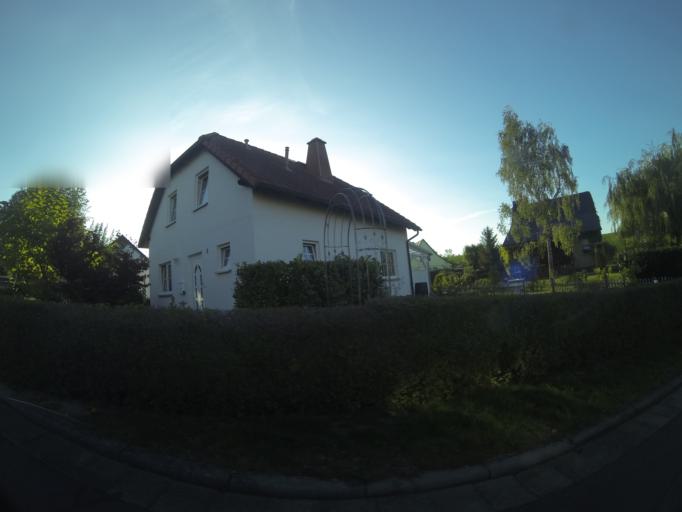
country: DE
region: Thuringia
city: Schmolln
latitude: 50.8915
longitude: 12.3715
